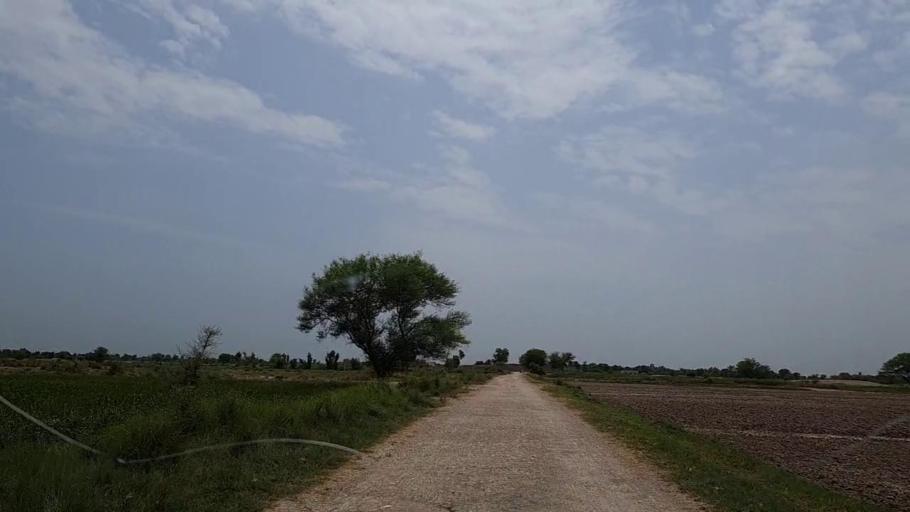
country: PK
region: Sindh
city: Tharu Shah
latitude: 26.9113
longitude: 68.0792
